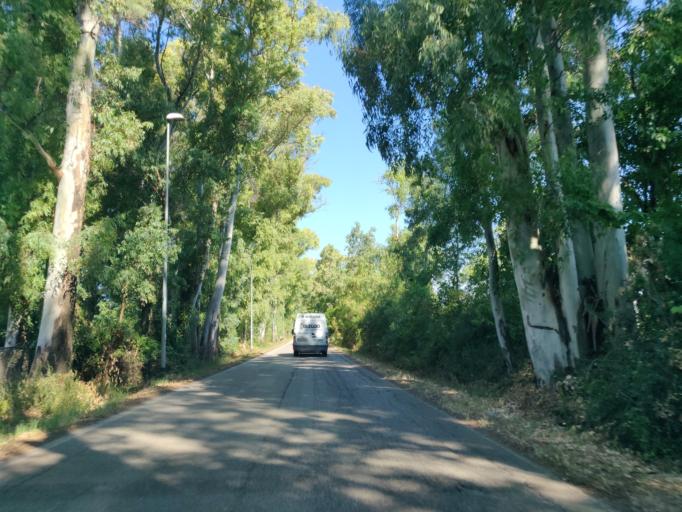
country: IT
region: Latium
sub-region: Citta metropolitana di Roma Capitale
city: Aurelia
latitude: 42.1584
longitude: 11.7509
